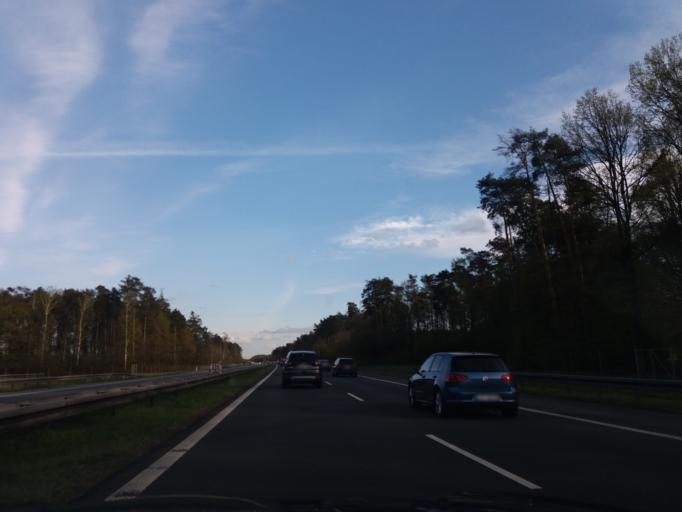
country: PL
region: Opole Voivodeship
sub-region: Powiat brzeski
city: Lewin Brzeski
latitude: 50.6977
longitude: 17.6222
